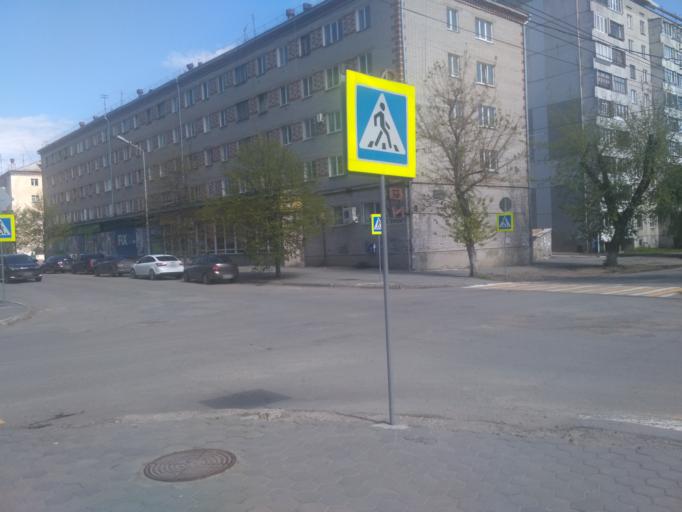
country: RU
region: Kurgan
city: Kurgan
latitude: 55.4325
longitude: 65.3405
